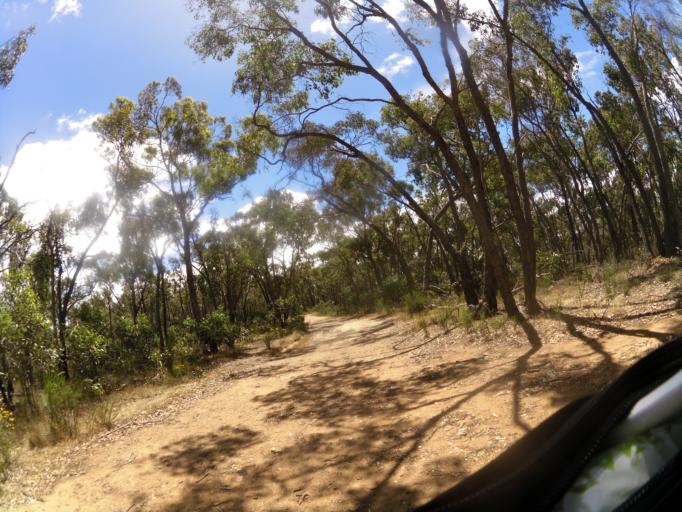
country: AU
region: Victoria
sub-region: Mount Alexander
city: Castlemaine
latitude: -37.0703
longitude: 144.2640
